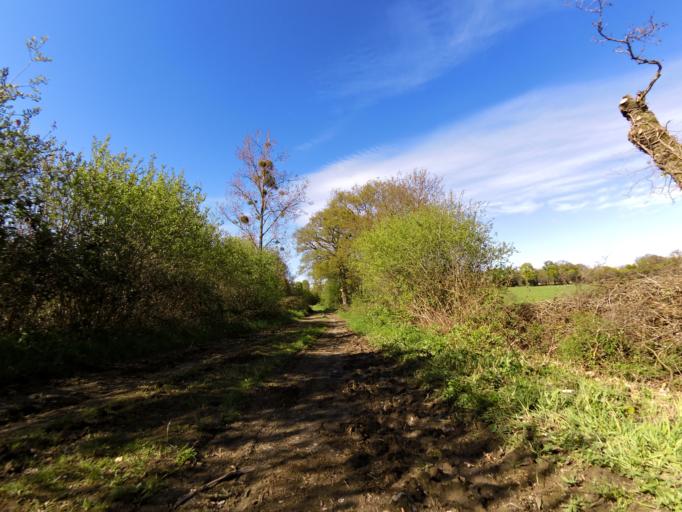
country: FR
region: Brittany
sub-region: Departement d'Ille-et-Vilaine
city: Pance
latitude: 47.9054
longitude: -1.6128
